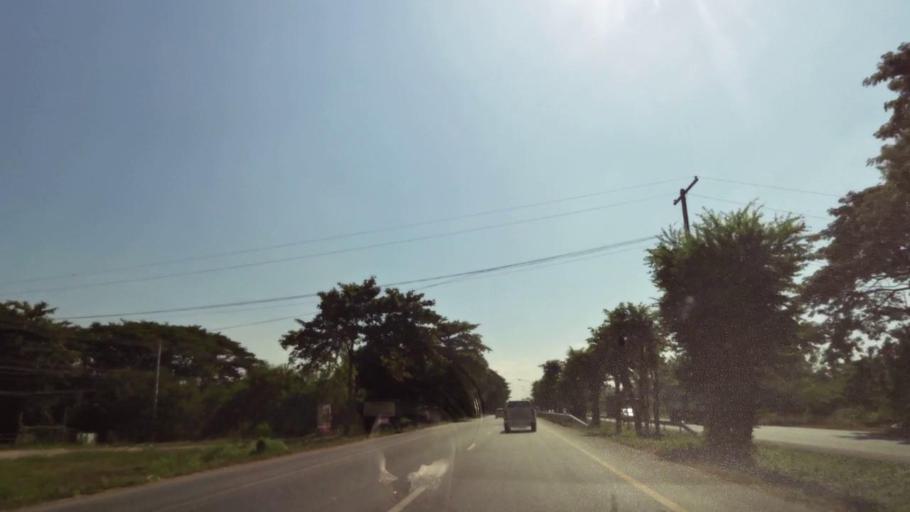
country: TH
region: Nakhon Sawan
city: Kao Liao
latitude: 15.7851
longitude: 100.1210
